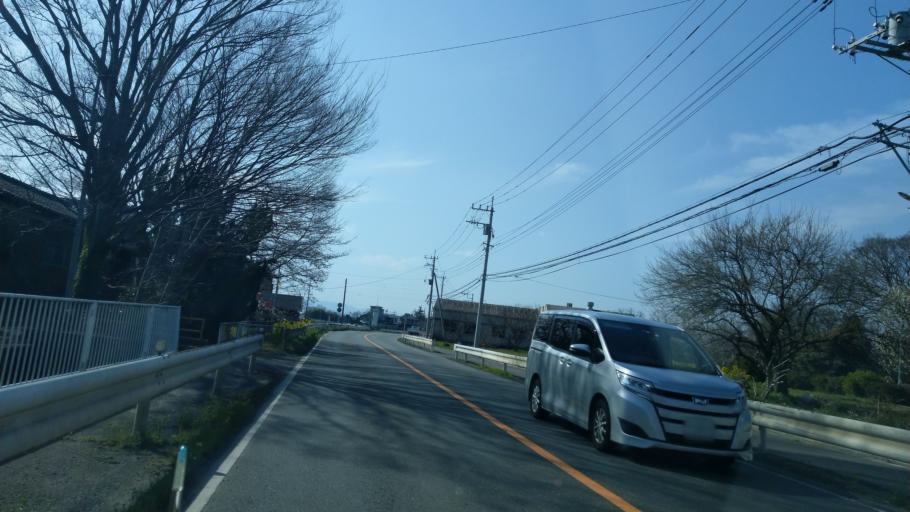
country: JP
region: Saitama
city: Okegawa
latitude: 35.9609
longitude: 139.5165
